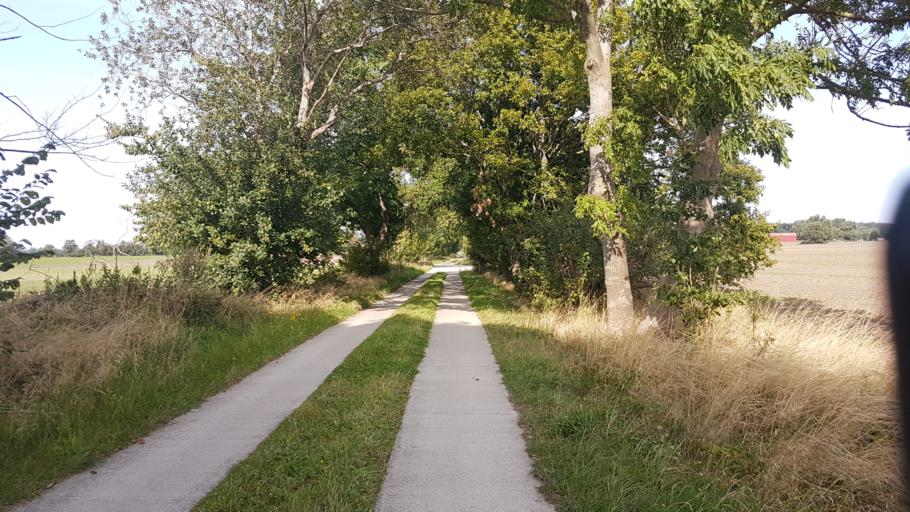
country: DE
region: Mecklenburg-Vorpommern
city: Samtens
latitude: 54.3980
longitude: 13.2596
